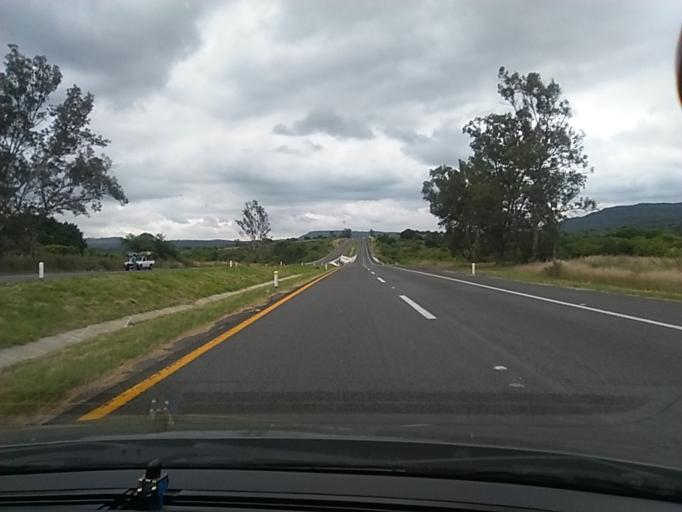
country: MX
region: Jalisco
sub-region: Zapotlanejo
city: La Mezquitera
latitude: 20.5521
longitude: -103.0479
